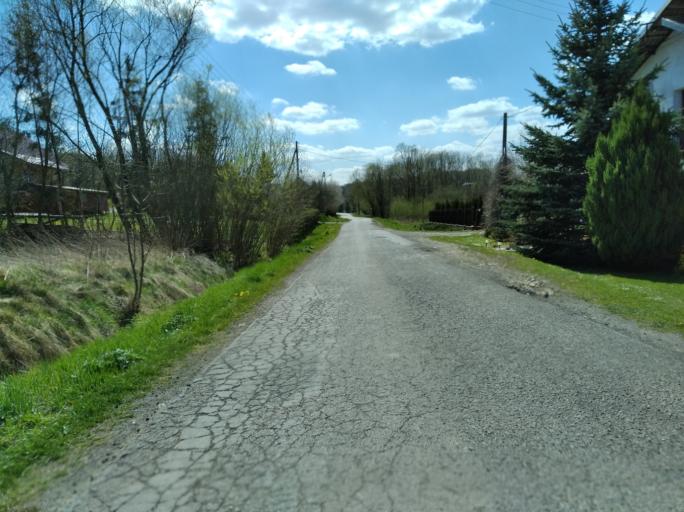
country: PL
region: Subcarpathian Voivodeship
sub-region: Powiat brzozowski
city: Domaradz
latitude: 49.7875
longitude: 21.9563
